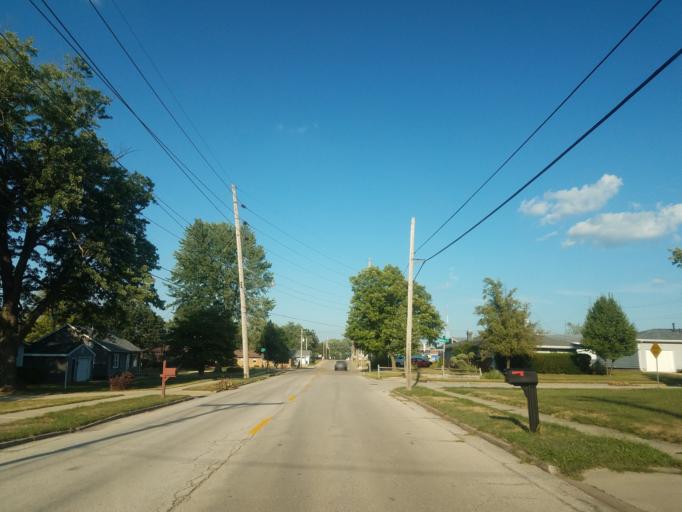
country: US
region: Illinois
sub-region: McLean County
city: Bloomington
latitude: 40.4635
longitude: -88.9779
